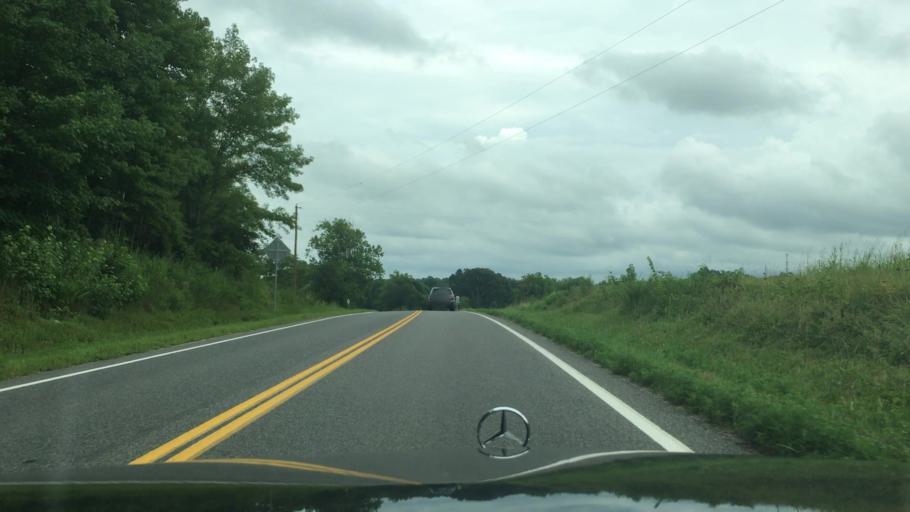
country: US
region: Virginia
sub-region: Nottoway County
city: Crewe
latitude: 37.2728
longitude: -78.1634
